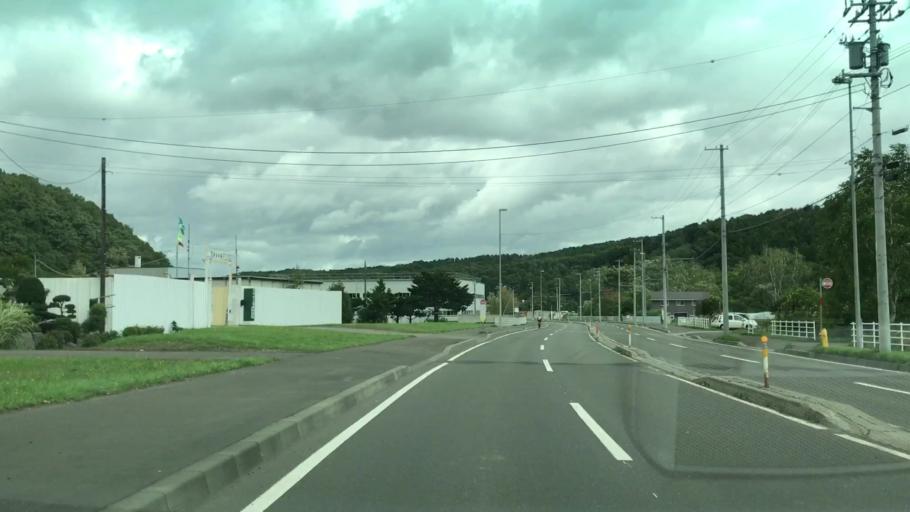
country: JP
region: Hokkaido
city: Kitahiroshima
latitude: 42.9576
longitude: 141.4545
